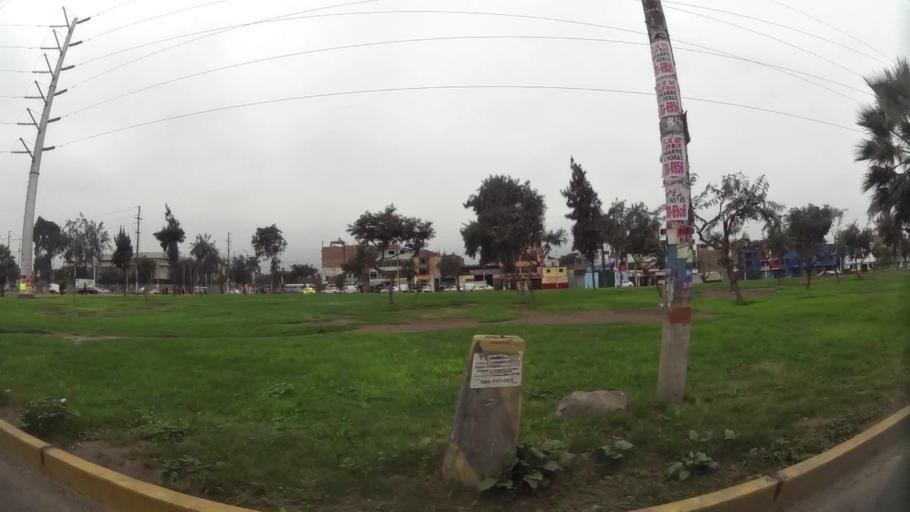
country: PE
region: Lima
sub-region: Lima
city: Independencia
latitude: -11.9787
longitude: -77.0778
